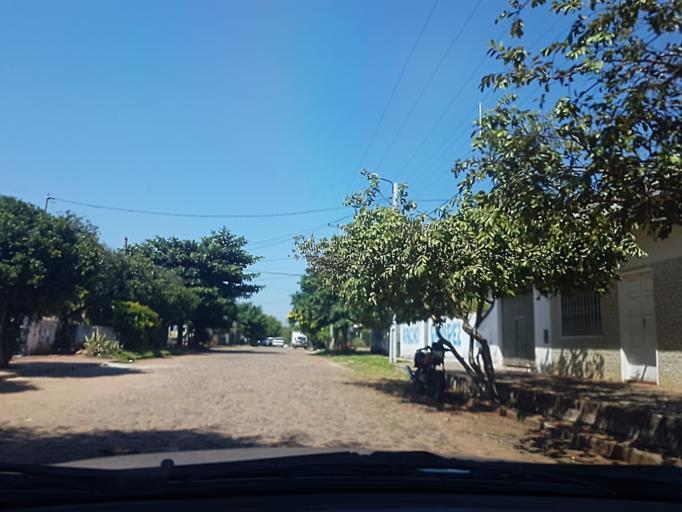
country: PY
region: Central
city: San Lorenzo
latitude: -25.2609
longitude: -57.4860
